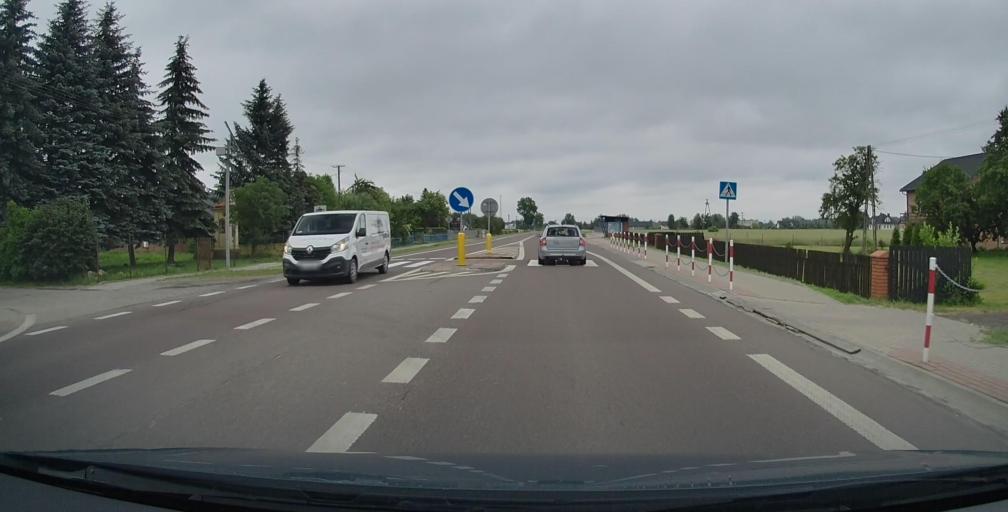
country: PL
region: Lublin Voivodeship
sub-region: Powiat bialski
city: Rzeczyca
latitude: 52.0327
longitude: 22.7024
